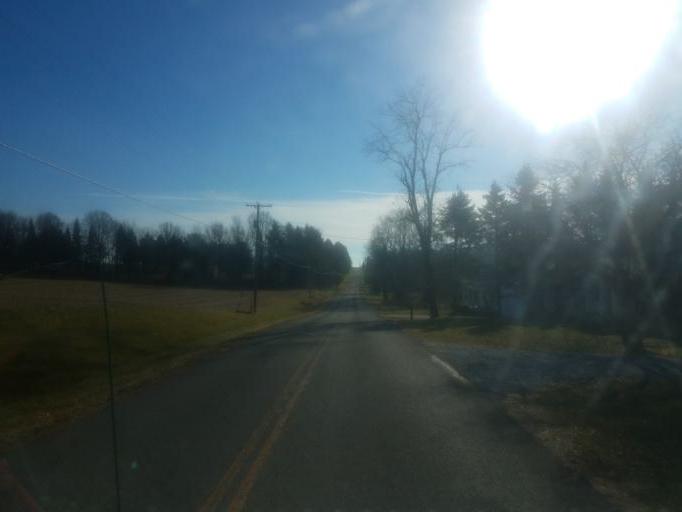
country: US
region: Ohio
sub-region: Richland County
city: Ontario
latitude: 40.7187
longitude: -82.5992
